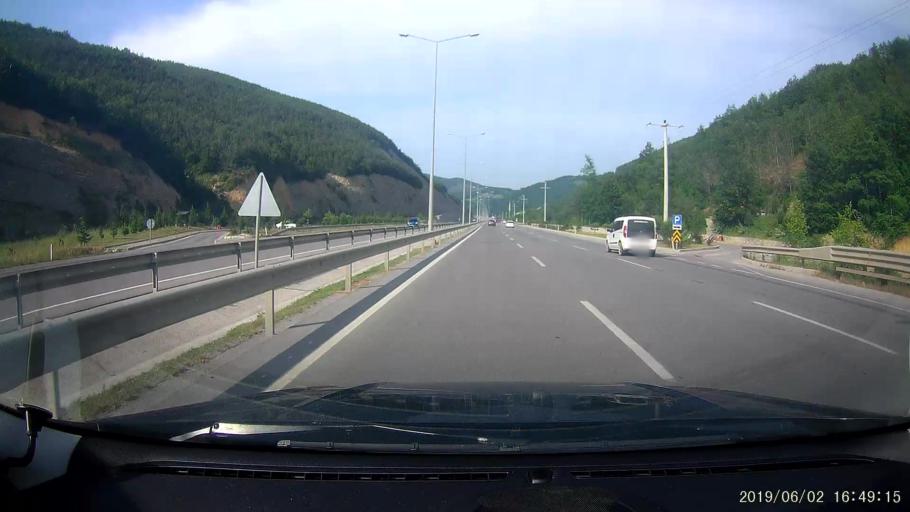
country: TR
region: Samsun
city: Taflan
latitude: 41.2348
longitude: 36.1575
